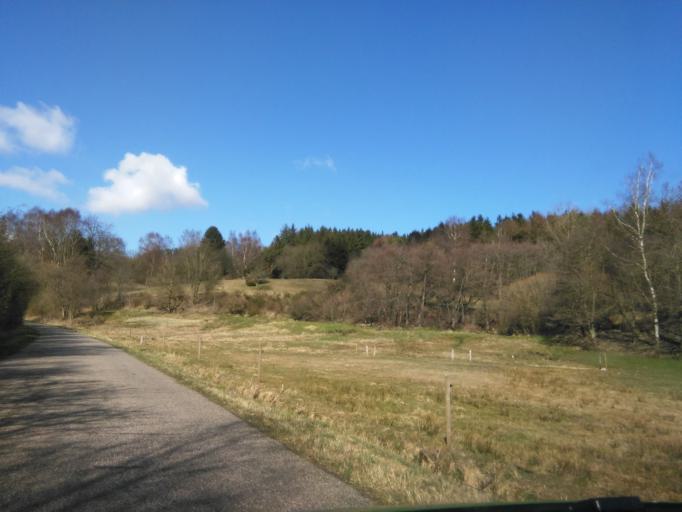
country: DK
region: Central Jutland
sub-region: Skanderborg Kommune
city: Ry
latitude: 56.1023
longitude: 9.7407
